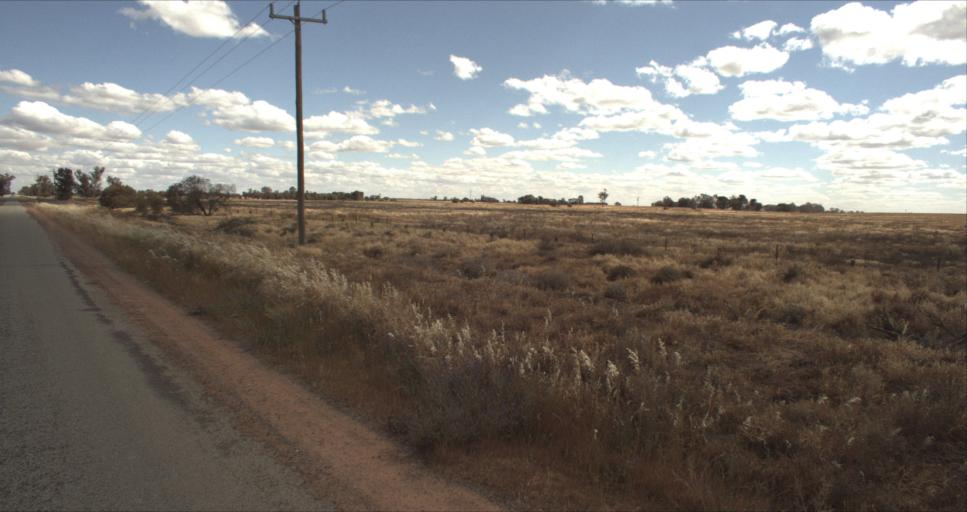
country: AU
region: New South Wales
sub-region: Leeton
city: Leeton
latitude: -34.4799
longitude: 146.2493
